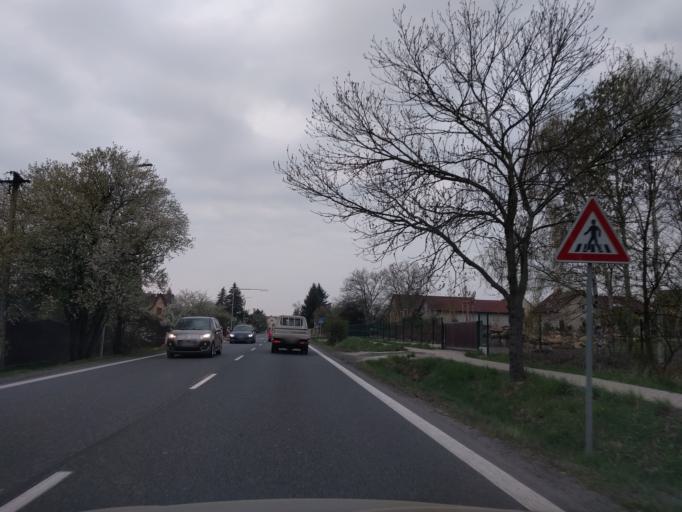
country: CZ
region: Central Bohemia
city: Mukarov
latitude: 49.9895
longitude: 14.7495
